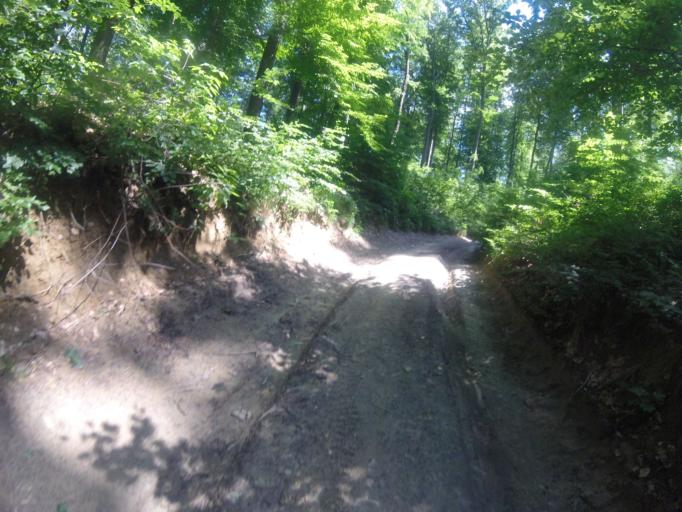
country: HU
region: Veszprem
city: Cseteny
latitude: 47.2626
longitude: 18.0128
